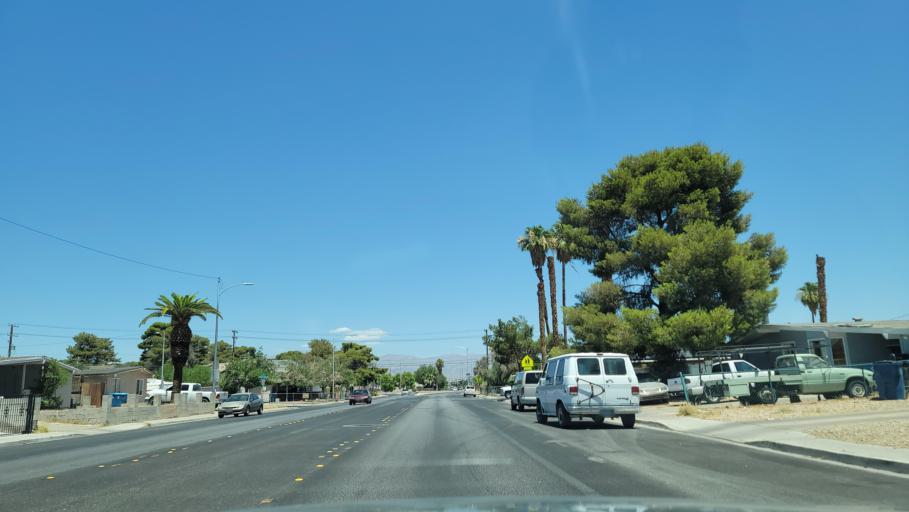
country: US
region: Nevada
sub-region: Clark County
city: Las Vegas
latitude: 36.1763
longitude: -115.1253
